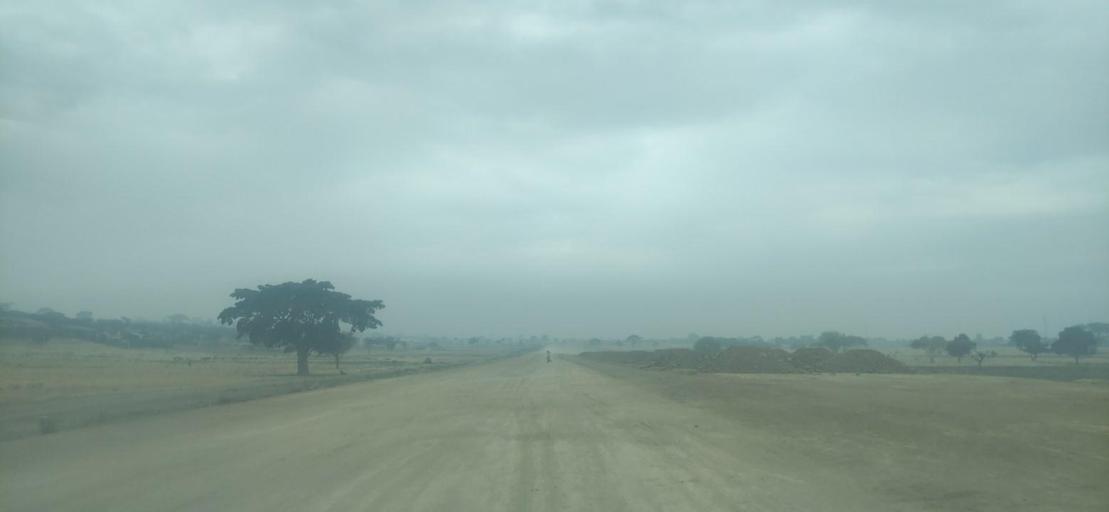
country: ET
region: Oromiya
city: Shashemene
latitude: 7.4055
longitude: 38.6608
